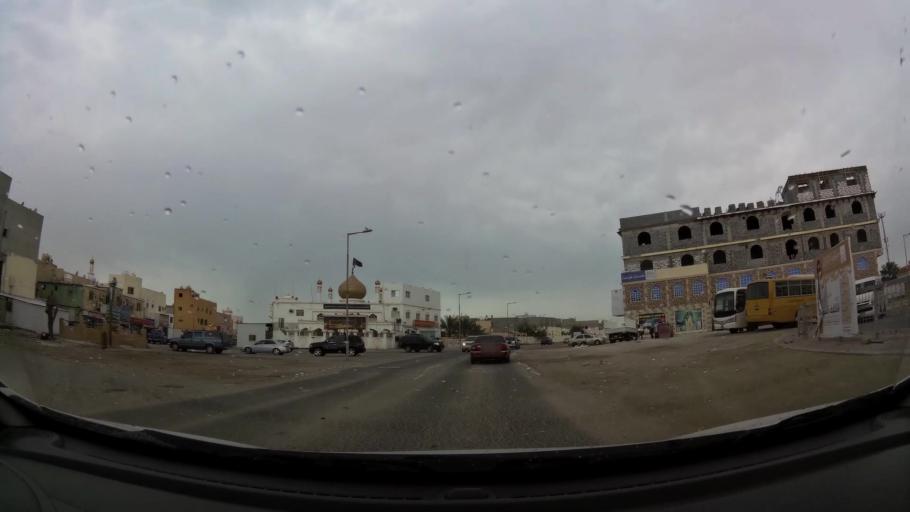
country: BH
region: Central Governorate
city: Madinat Hamad
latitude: 26.1271
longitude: 50.4775
